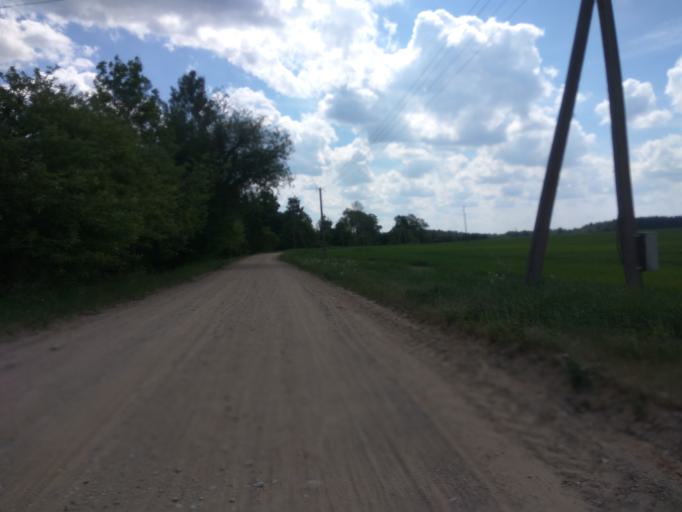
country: LV
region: Kuldigas Rajons
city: Kuldiga
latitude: 56.8931
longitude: 21.9702
